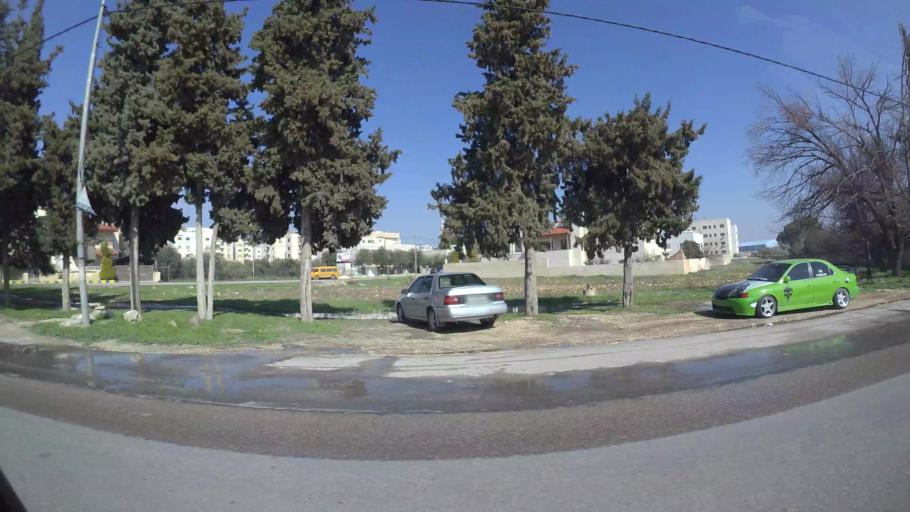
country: JO
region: Amman
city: Al Bunayyat ash Shamaliyah
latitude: 31.9028
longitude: 35.8758
